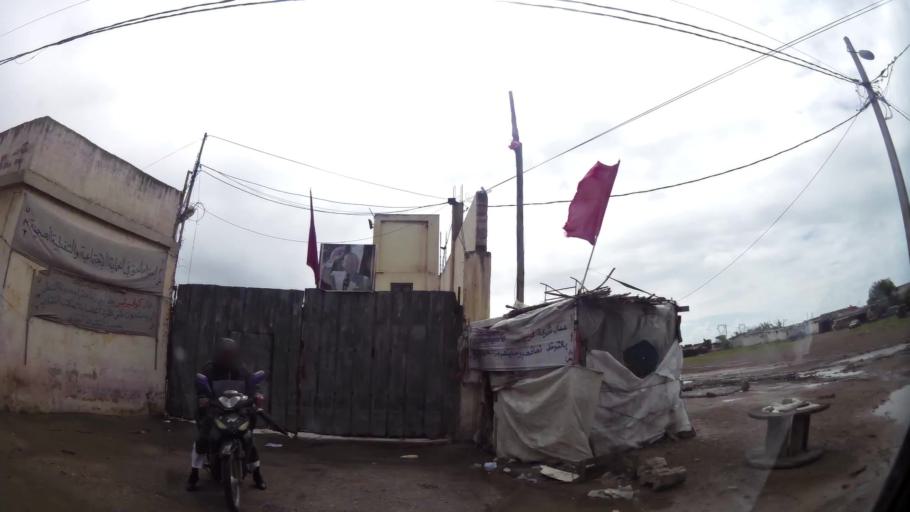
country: MA
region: Grand Casablanca
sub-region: Mediouna
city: Tit Mellil
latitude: 33.6390
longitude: -7.4746
